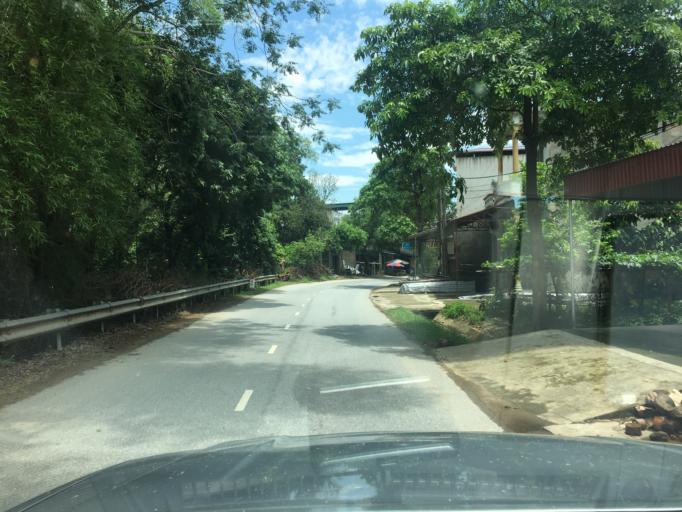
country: VN
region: Yen Bai
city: Son Thinh
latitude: 21.6512
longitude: 104.5010
